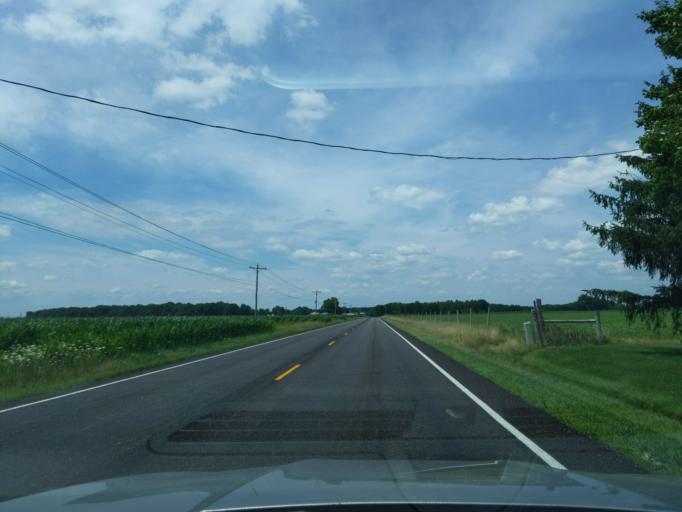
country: US
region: Indiana
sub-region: Ripley County
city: Osgood
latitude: 39.2357
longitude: -85.3419
